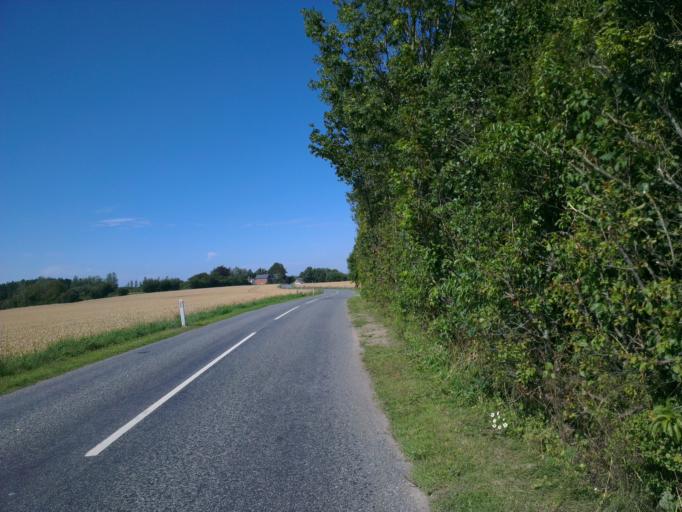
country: DK
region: Capital Region
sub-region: Frederikssund Kommune
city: Frederikssund
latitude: 55.8668
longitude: 12.0908
